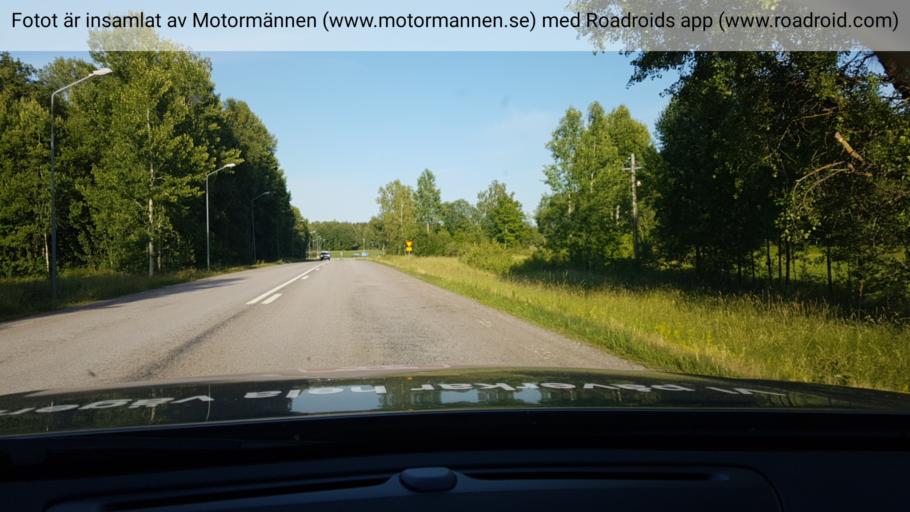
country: SE
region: Uppsala
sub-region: Osthammars Kommun
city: Gimo
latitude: 60.1650
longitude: 18.1877
